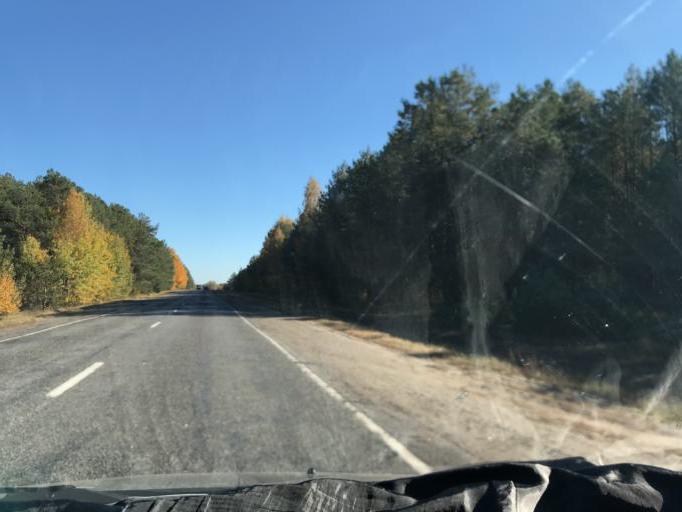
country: BY
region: Gomel
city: Kalinkavichy
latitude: 52.3815
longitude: 29.3341
